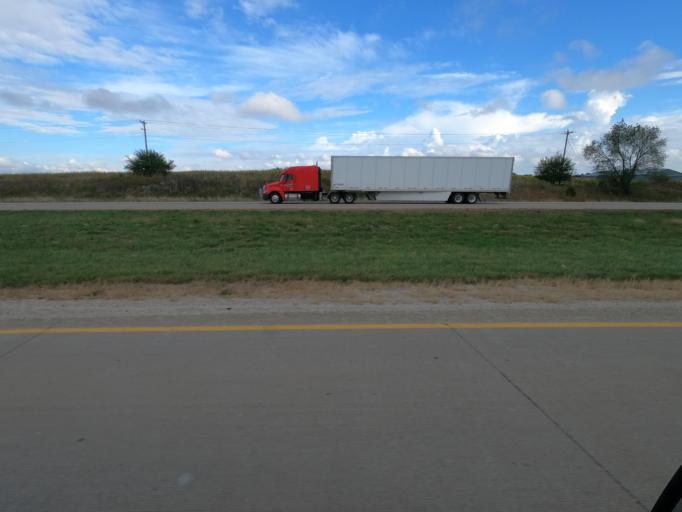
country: US
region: Illinois
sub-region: Hancock County
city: Nauvoo
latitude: 40.7144
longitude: -91.5637
